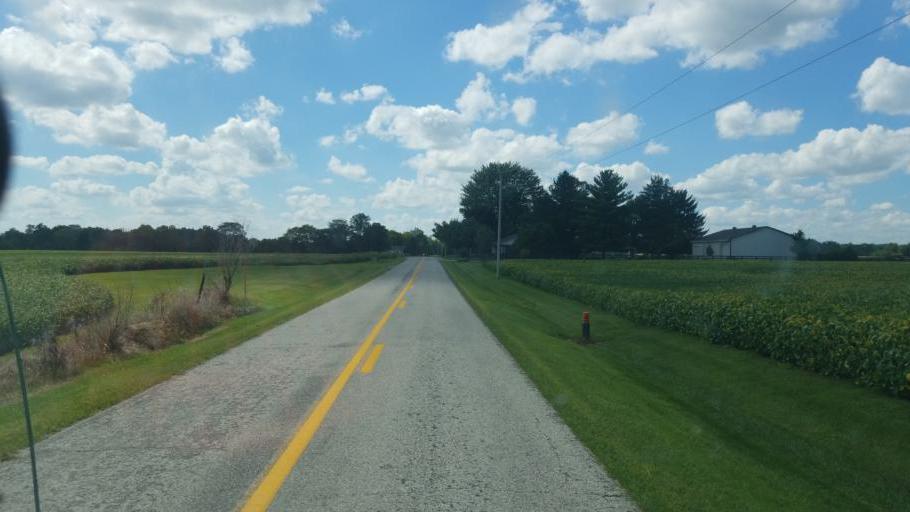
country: US
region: Ohio
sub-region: Union County
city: Richwood
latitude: 40.3505
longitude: -83.2315
